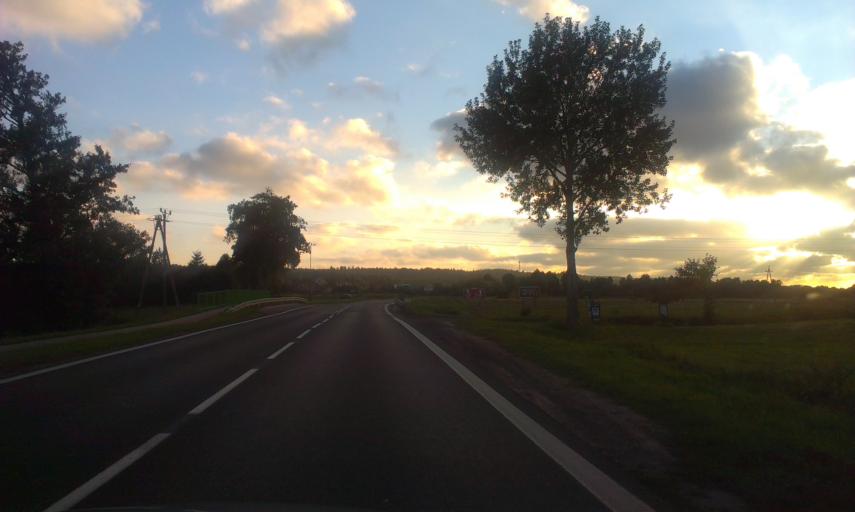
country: PL
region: West Pomeranian Voivodeship
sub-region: Powiat koszalinski
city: Sianow
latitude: 54.2226
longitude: 16.2854
